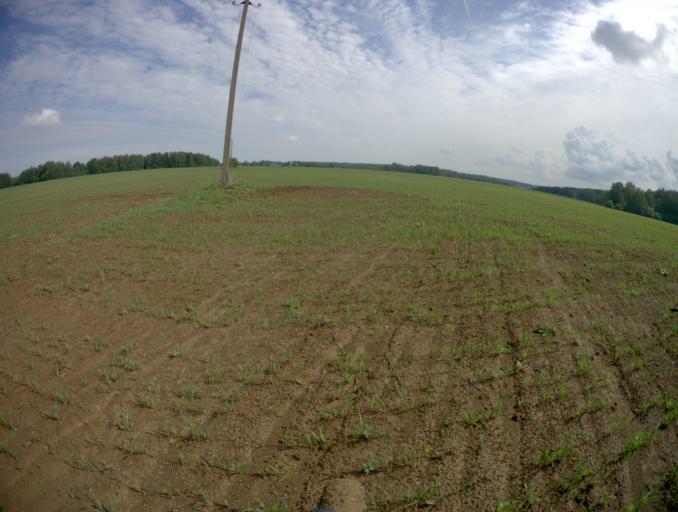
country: RU
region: Vladimir
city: Lakinsk
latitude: 56.0958
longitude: 39.9162
